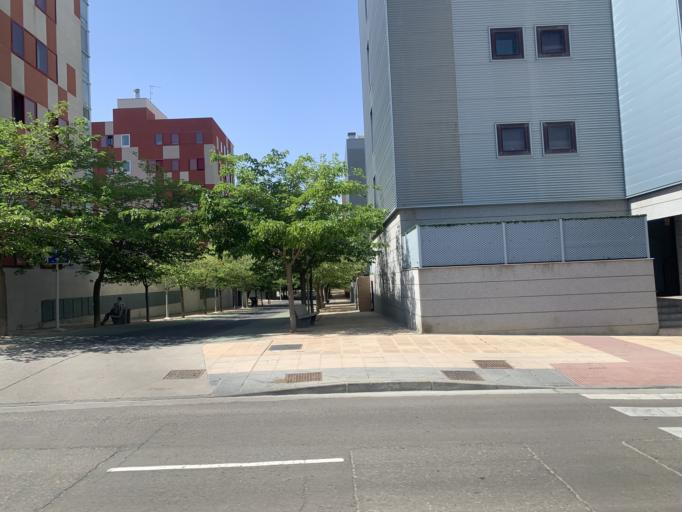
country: ES
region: Aragon
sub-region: Provincia de Zaragoza
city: Montecanal
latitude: 41.6232
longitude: -0.9319
